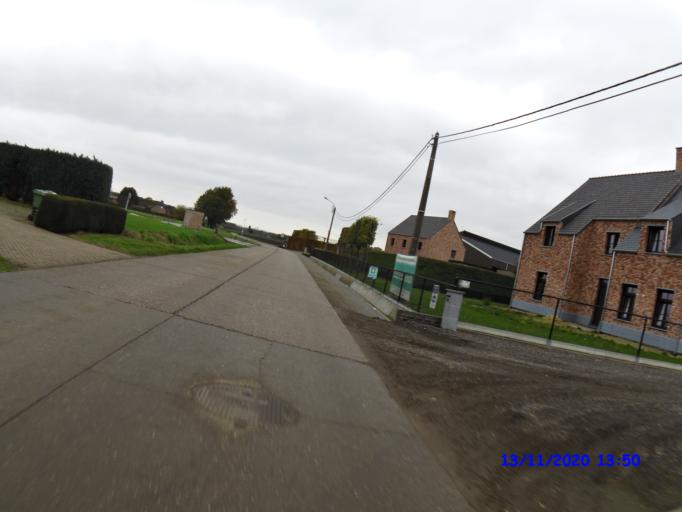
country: BE
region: Flanders
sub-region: Provincie Antwerpen
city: Kasterlee
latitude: 51.2762
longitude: 4.9749
